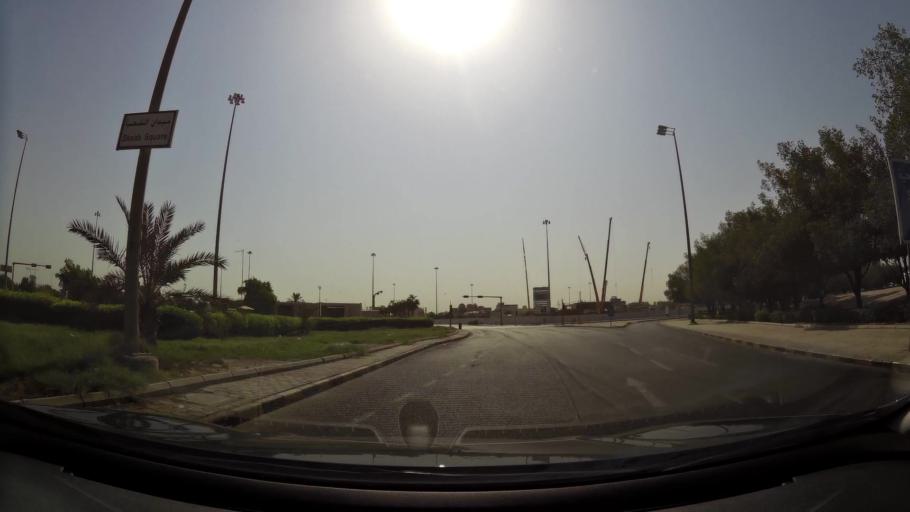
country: KW
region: Al Asimah
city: Kuwait City
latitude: 29.3669
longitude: 47.9895
